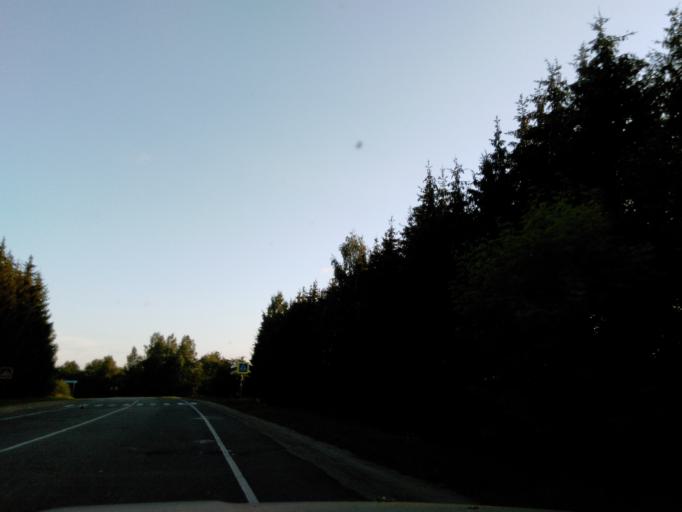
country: RU
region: Tverskaya
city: Konakovo
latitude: 56.6531
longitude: 36.7102
